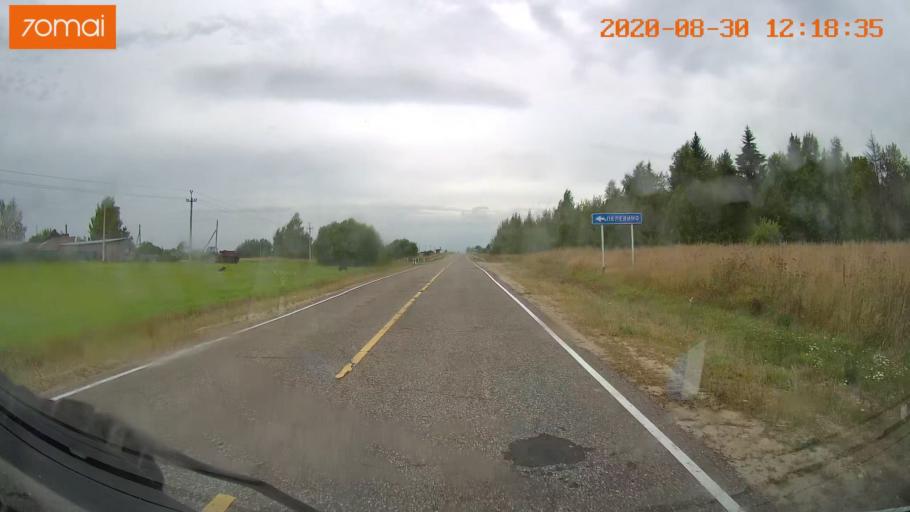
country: RU
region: Ivanovo
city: Yur'yevets
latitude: 57.3233
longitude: 42.9484
